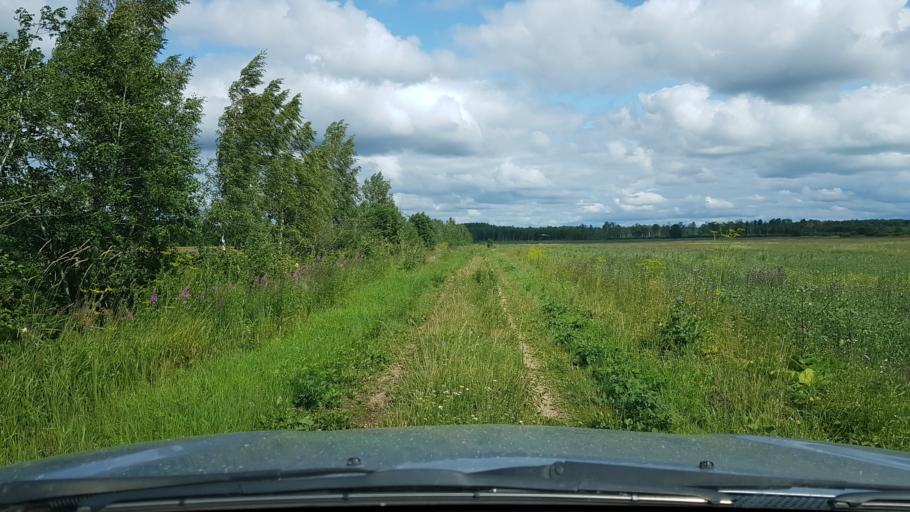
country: EE
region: Ida-Virumaa
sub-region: Narva-Joesuu linn
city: Narva-Joesuu
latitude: 59.3832
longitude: 27.9359
